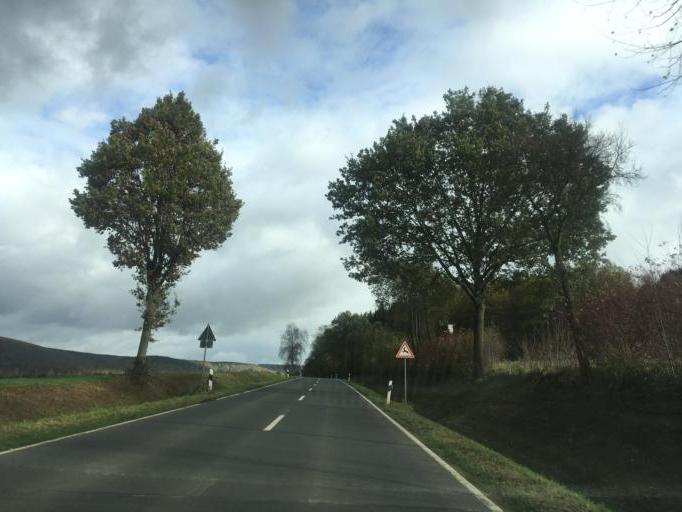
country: DE
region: Lower Saxony
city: Bodenfelde
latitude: 51.6464
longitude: 9.5243
